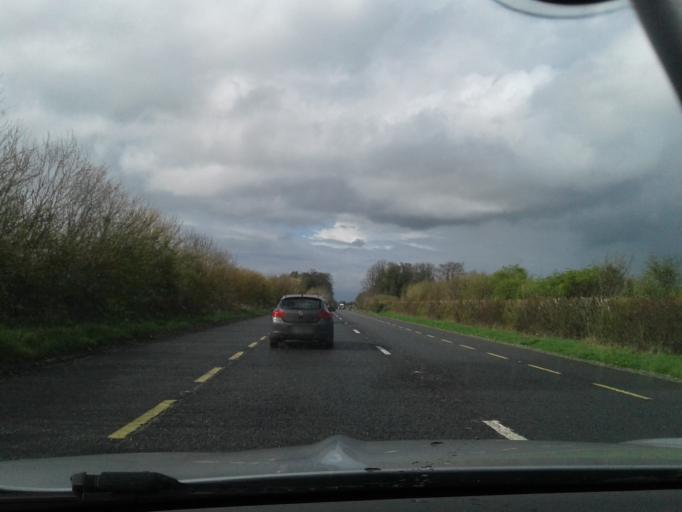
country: IE
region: Leinster
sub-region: Lu
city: Ardee
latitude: 53.8842
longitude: -6.5707
